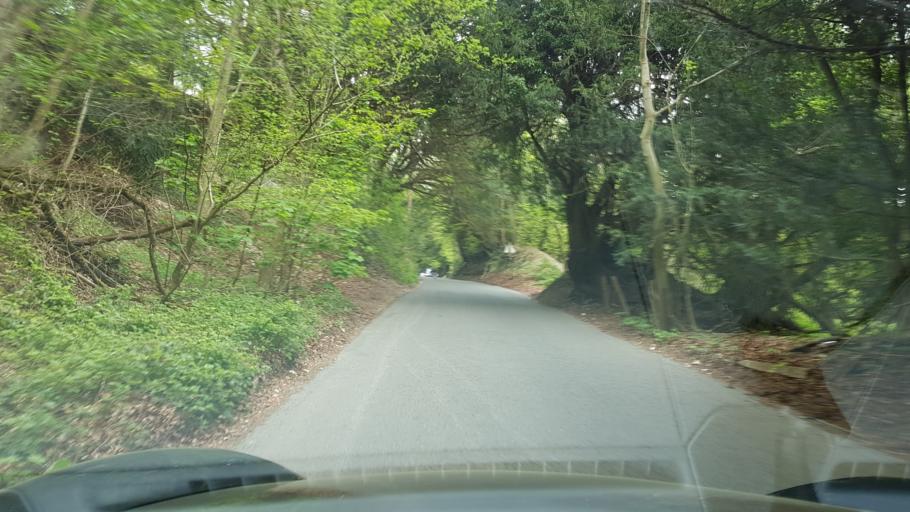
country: GB
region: England
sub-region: Surrey
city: East Horsley
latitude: 51.2265
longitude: -0.4090
